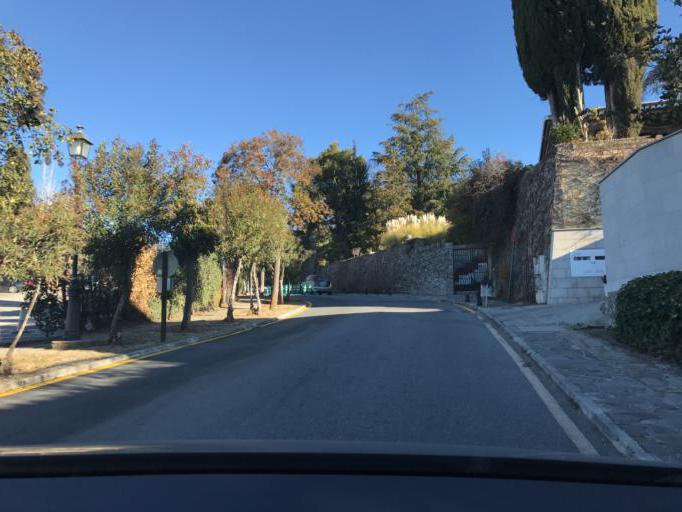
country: ES
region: Andalusia
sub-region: Provincia de Granada
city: Huetor Vega
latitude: 37.1610
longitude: -3.5792
